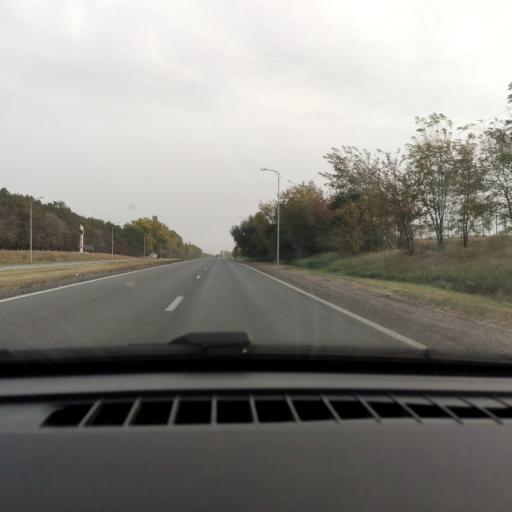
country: RU
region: Belgorod
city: Razumnoye
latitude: 50.6641
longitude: 36.7051
